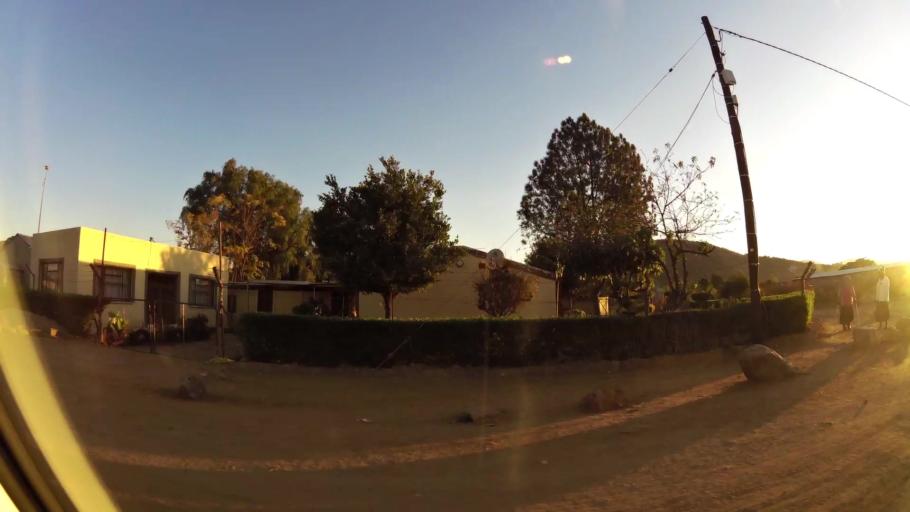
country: ZA
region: Limpopo
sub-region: Waterberg District Municipality
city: Mokopane
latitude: -24.1478
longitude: 28.9774
